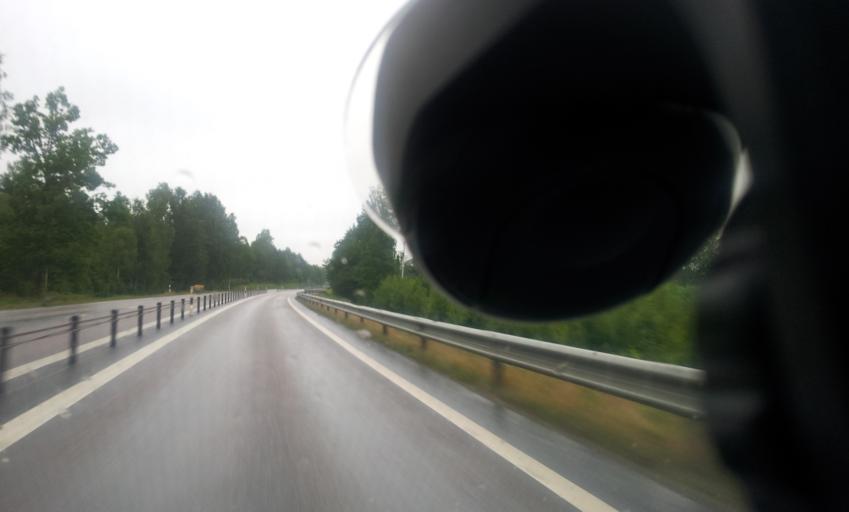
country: SE
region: Kalmar
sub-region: Vasterviks Kommun
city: Forserum
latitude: 58.0502
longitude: 16.5246
